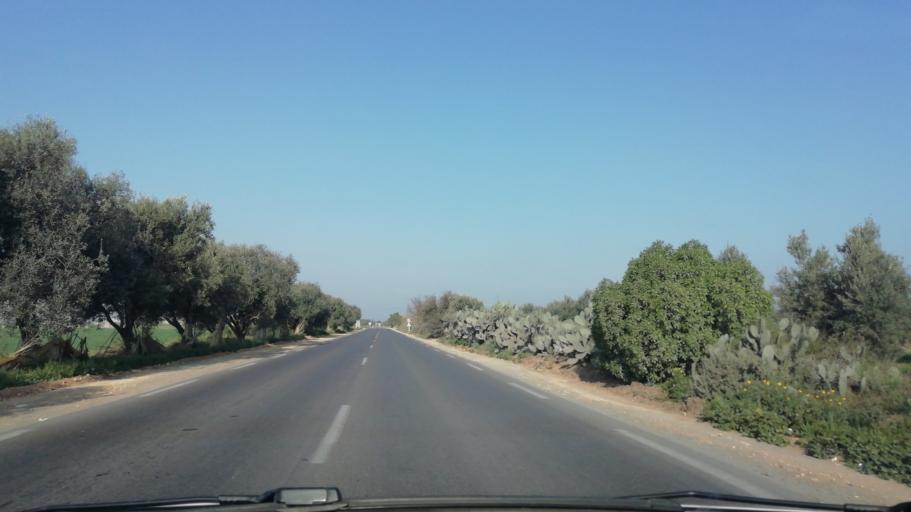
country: DZ
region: Mostaganem
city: Mostaganem
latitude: 35.7552
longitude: 0.1124
